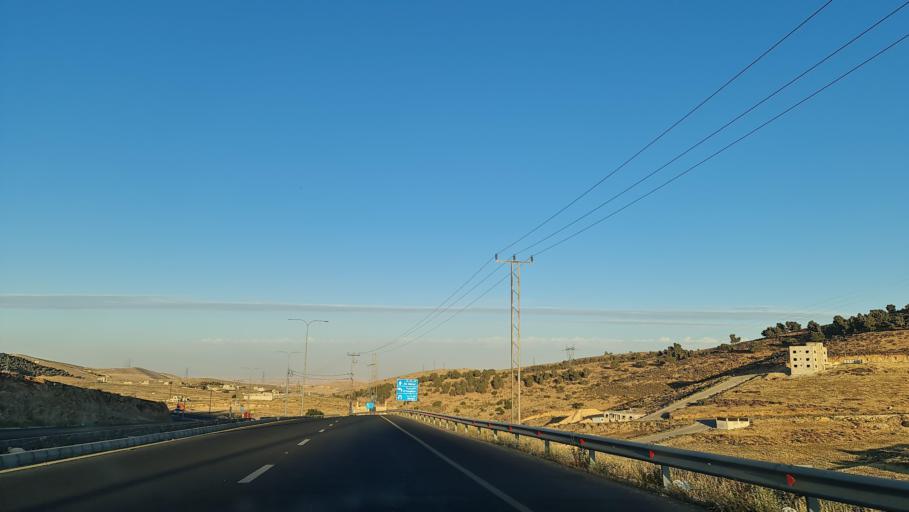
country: JO
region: Zarqa
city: Russeifa
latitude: 32.0924
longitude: 35.9699
